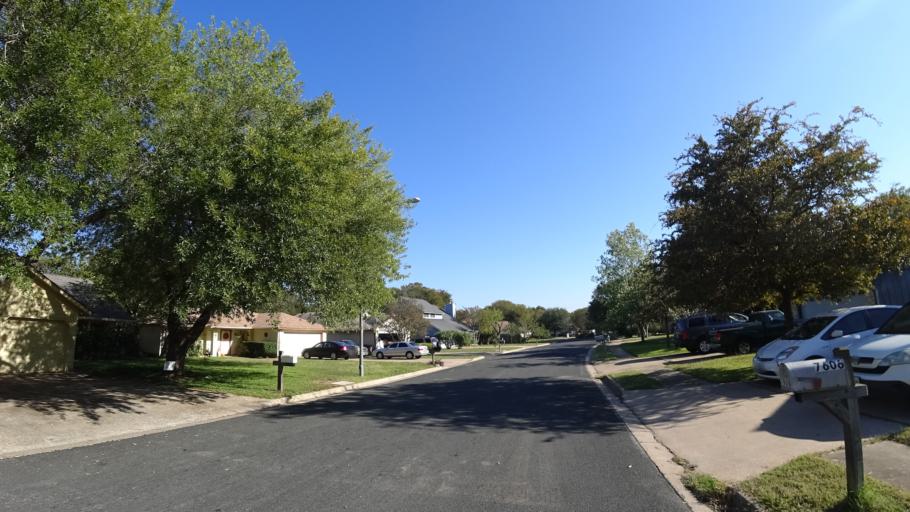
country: US
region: Texas
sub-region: Travis County
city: Shady Hollow
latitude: 30.2146
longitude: -97.8492
